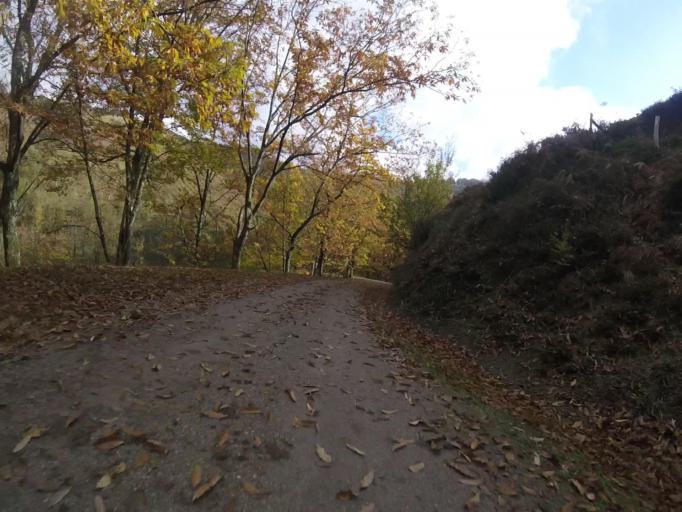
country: ES
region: Navarre
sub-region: Provincia de Navarra
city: Goizueta
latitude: 43.2067
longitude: -1.8310
